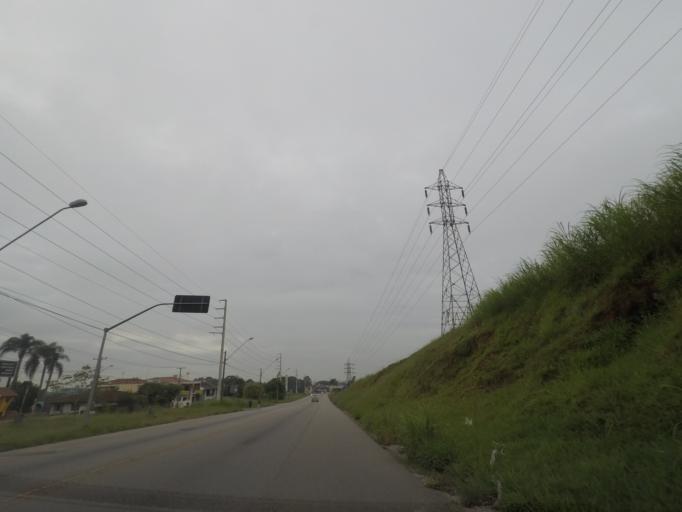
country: BR
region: Parana
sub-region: Curitiba
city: Curitiba
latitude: -25.3769
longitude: -49.2738
